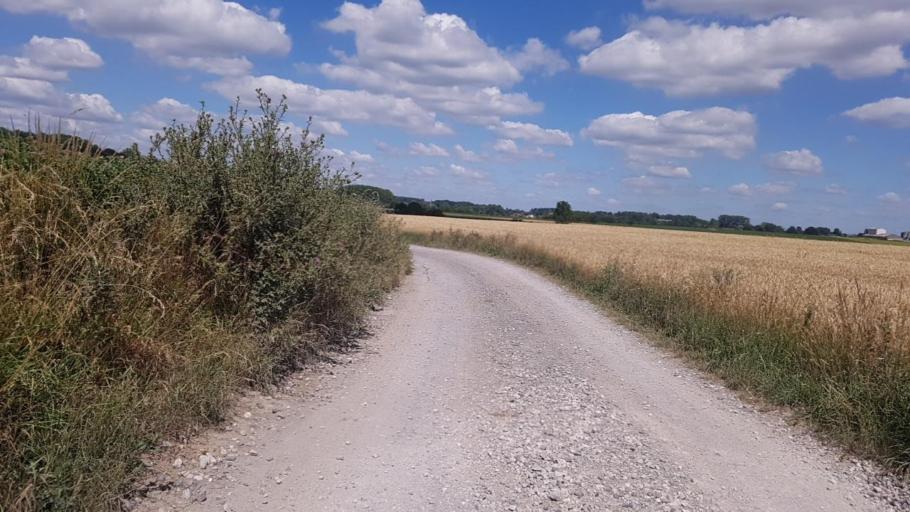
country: BE
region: Wallonia
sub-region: Province du Hainaut
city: Thuin
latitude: 50.3136
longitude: 4.3502
